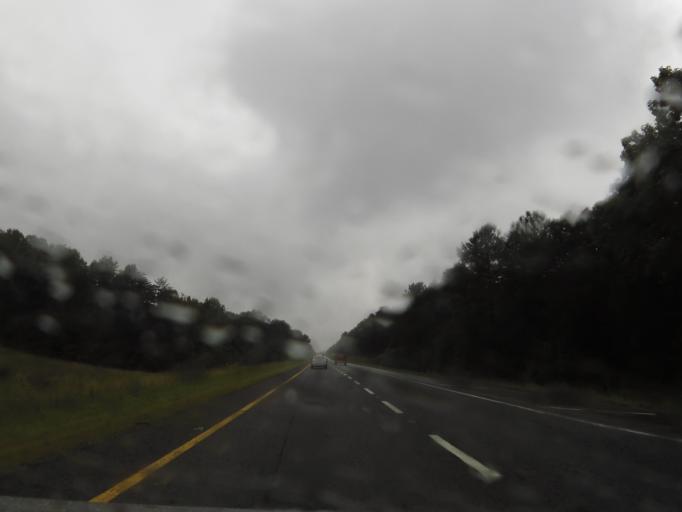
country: US
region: Tennessee
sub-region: Bradley County
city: Hopewell
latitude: 35.2733
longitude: -84.8245
